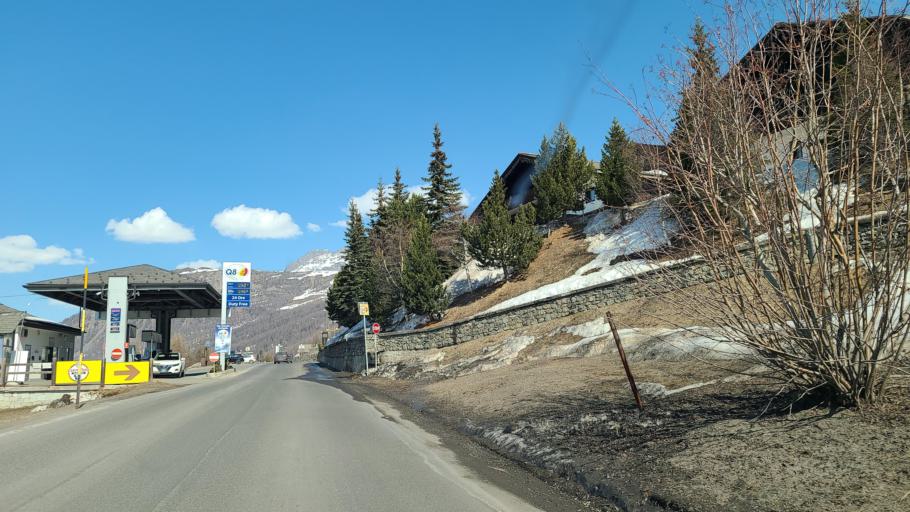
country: IT
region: Lombardy
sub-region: Provincia di Sondrio
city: Livigno
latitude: 46.5271
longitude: 10.1349
